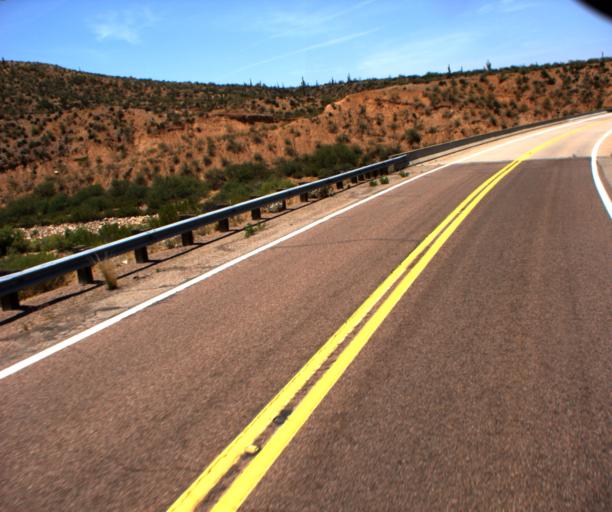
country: US
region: Arizona
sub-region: Gila County
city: Tonto Basin
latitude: 33.7275
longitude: -111.2113
